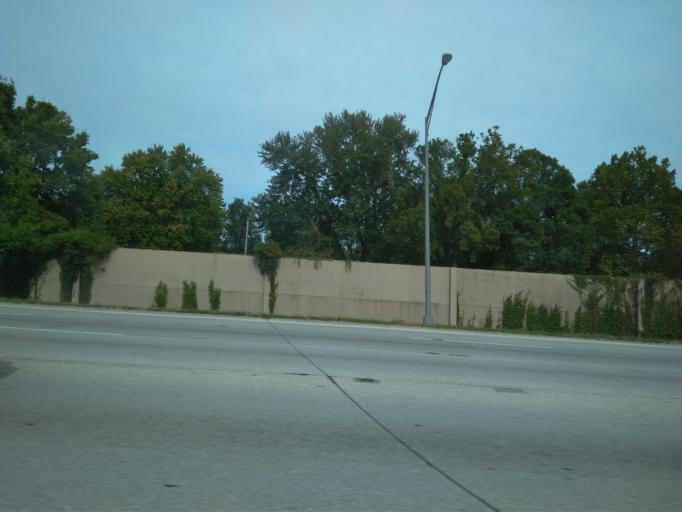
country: US
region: Kentucky
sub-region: Jefferson County
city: West Buechel
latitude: 38.2175
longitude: -85.6594
